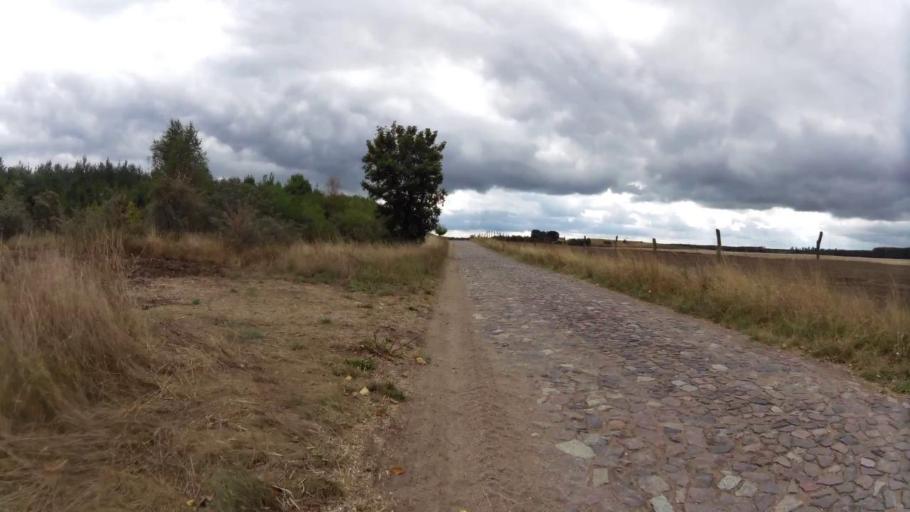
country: PL
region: West Pomeranian Voivodeship
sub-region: Powiat mysliborski
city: Debno
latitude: 52.8375
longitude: 14.7150
